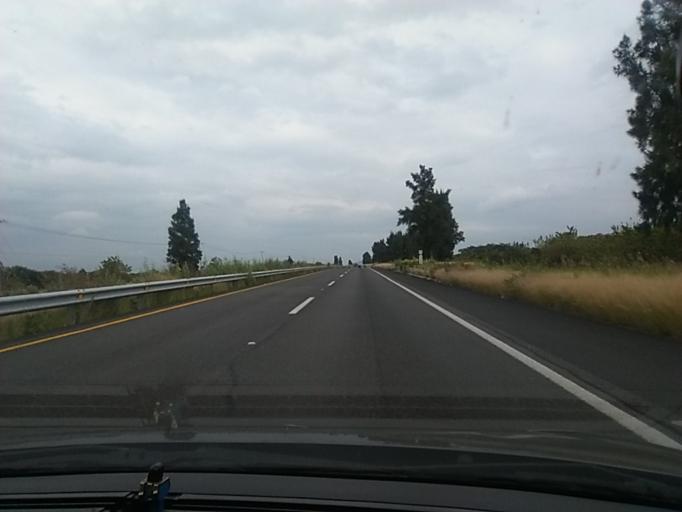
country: MX
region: Michoacan
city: Ecuandureo
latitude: 20.1693
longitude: -102.1423
